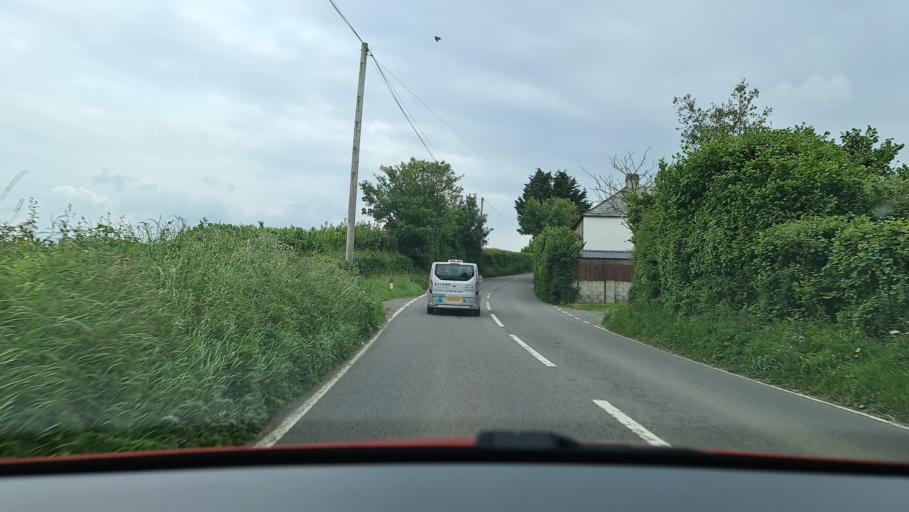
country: GB
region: England
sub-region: Cornwall
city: Poundstock
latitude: 50.7892
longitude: -4.5335
